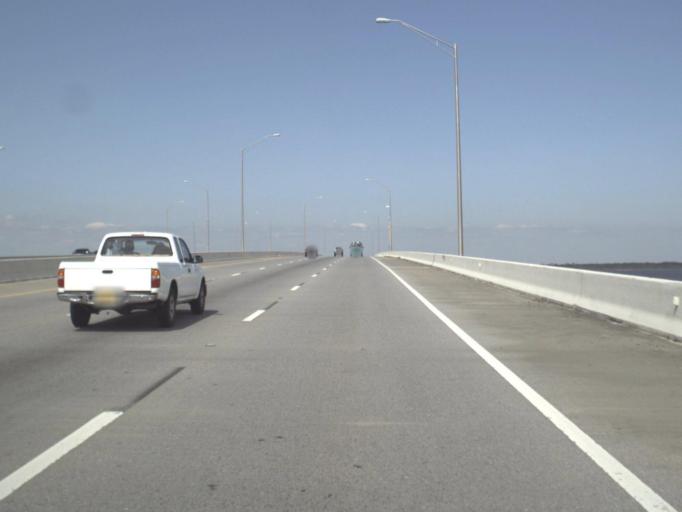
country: US
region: Florida
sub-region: Escambia County
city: Ferry Pass
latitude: 30.5140
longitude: -87.1508
